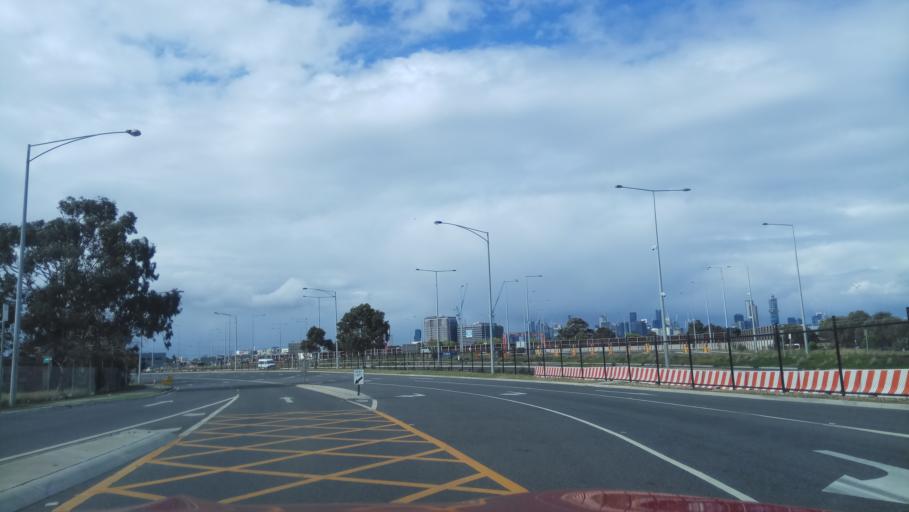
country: AU
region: Victoria
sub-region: Hobsons Bay
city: Williamstown
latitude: -37.8408
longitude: 144.9121
